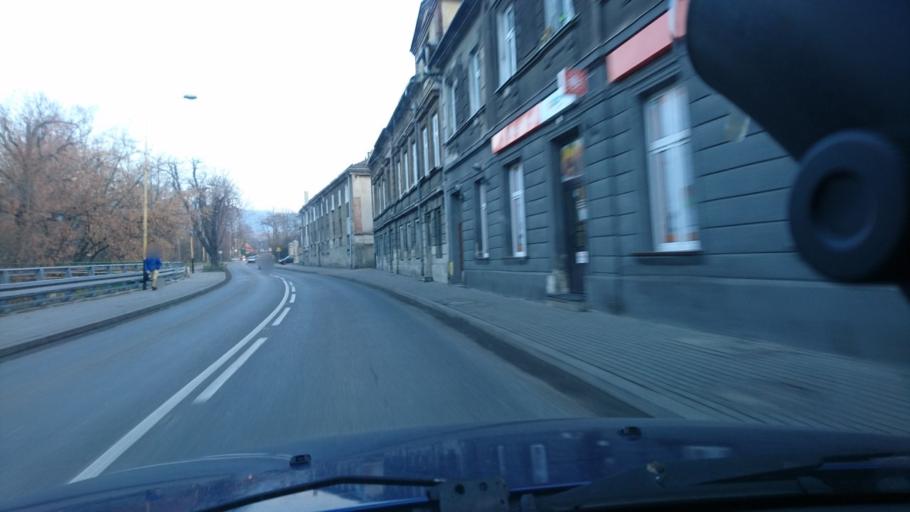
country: PL
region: Silesian Voivodeship
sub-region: Bielsko-Biala
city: Bielsko-Biala
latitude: 49.8186
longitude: 19.0636
